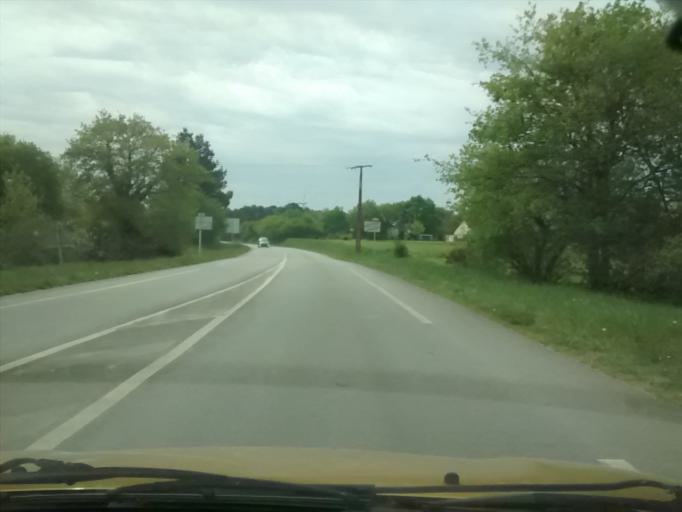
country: FR
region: Brittany
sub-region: Departement du Morbihan
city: Berric
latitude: 47.6142
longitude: -2.5405
